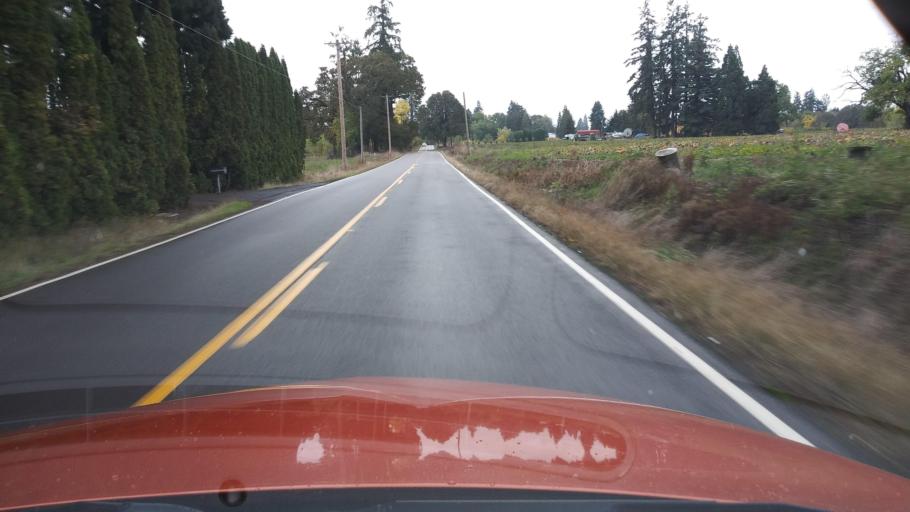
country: US
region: Oregon
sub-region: Washington County
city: Forest Grove
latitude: 45.5354
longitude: -123.0871
